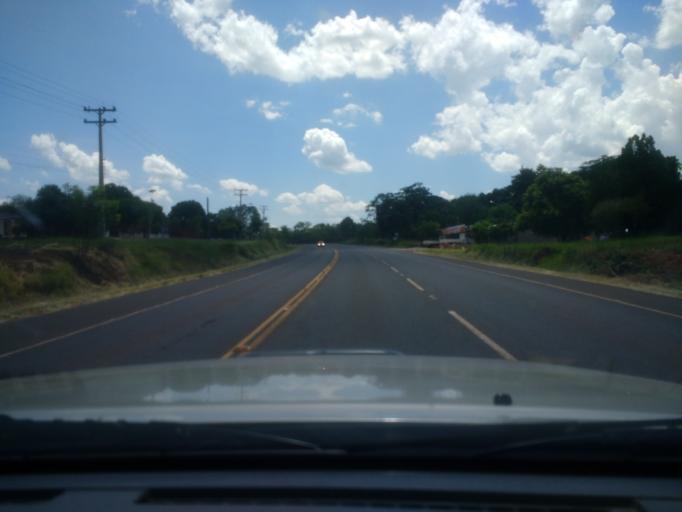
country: PY
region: San Pedro
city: Guayaybi
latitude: -24.5951
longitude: -56.5095
